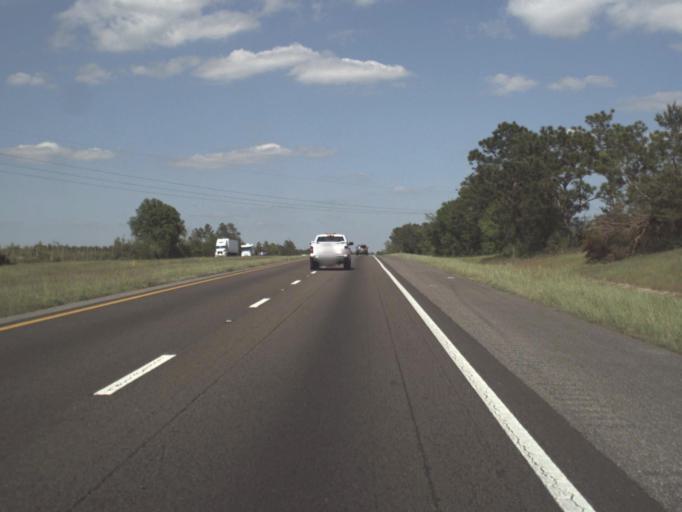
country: US
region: Florida
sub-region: Santa Rosa County
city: East Milton
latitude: 30.6662
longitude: -86.8567
